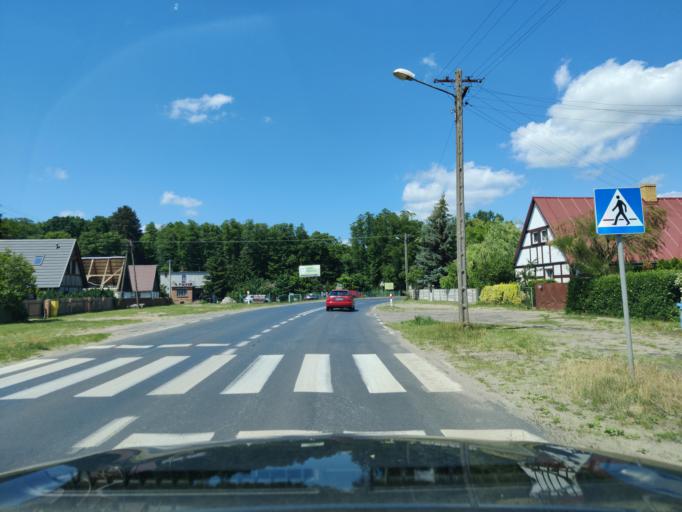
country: PL
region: Greater Poland Voivodeship
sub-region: Powiat grodziski
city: Jablonna
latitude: 52.2161
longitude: 16.1083
